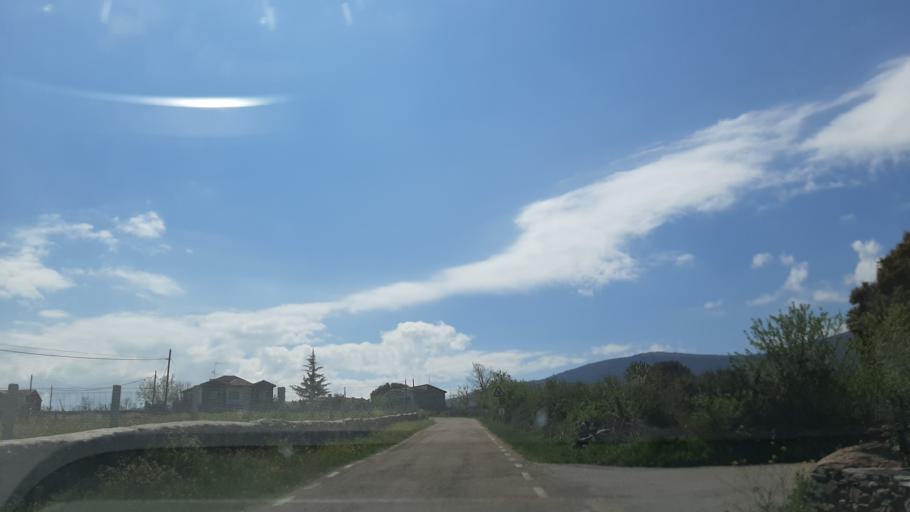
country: ES
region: Castille and Leon
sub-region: Provincia de Salamanca
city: Navarredonda de la Rinconada
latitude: 40.6154
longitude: -6.0195
